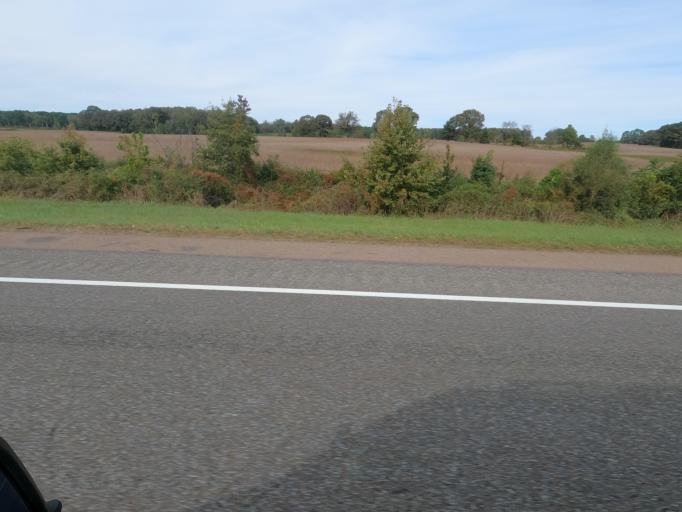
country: US
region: Tennessee
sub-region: Henderson County
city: Lexington
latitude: 35.7772
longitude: -88.4271
